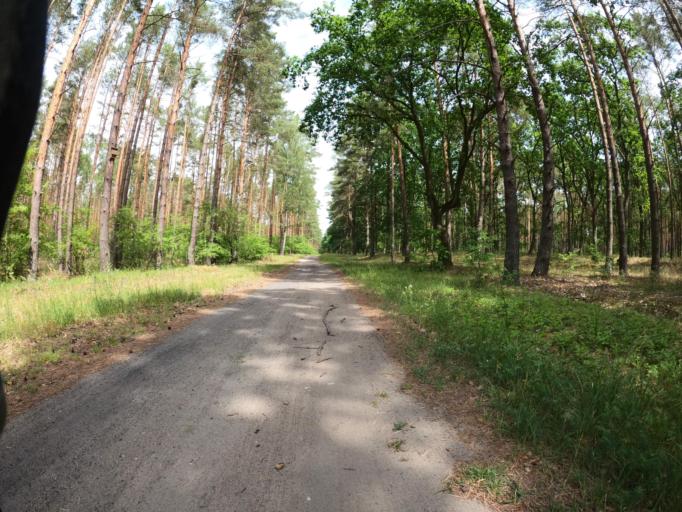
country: DE
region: Brandenburg
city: Zechin
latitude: 52.6822
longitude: 14.4903
